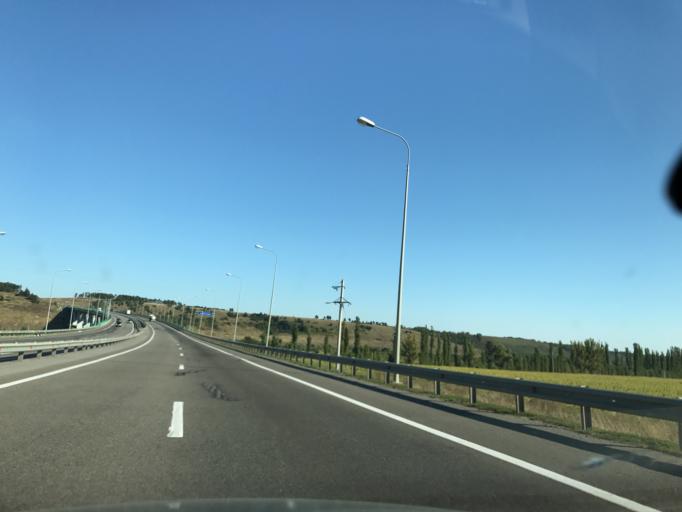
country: RU
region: Rostov
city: Tarasovskiy
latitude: 48.7245
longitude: 40.4054
